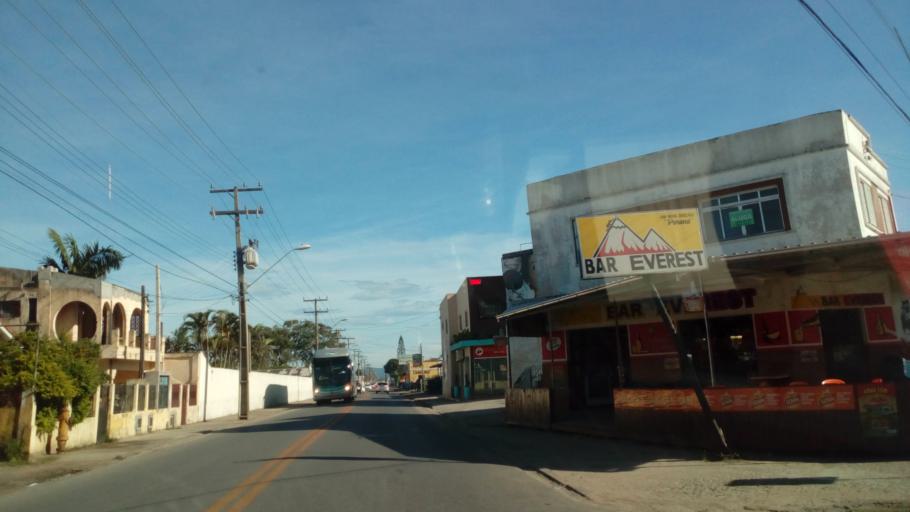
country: BR
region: Santa Catarina
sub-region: Laguna
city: Laguna
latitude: -28.4749
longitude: -48.7838
